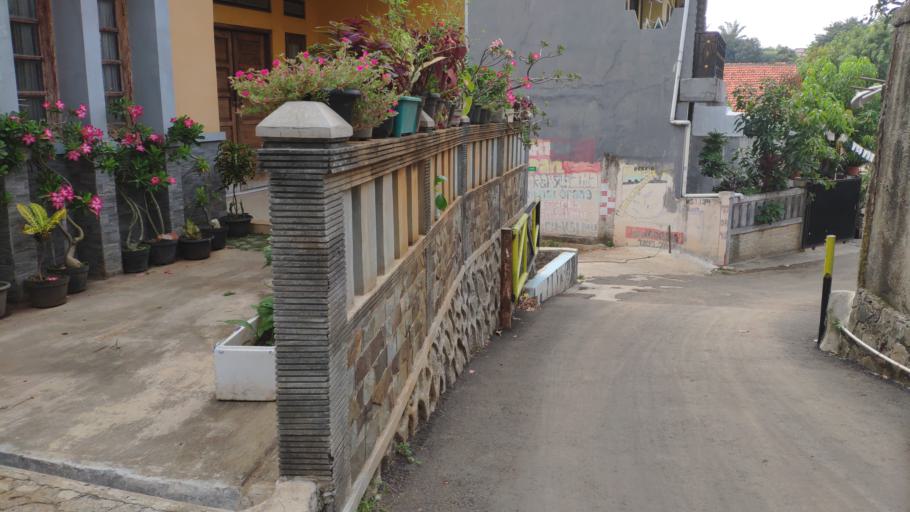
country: ID
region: West Java
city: Depok
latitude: -6.3430
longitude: 106.8076
